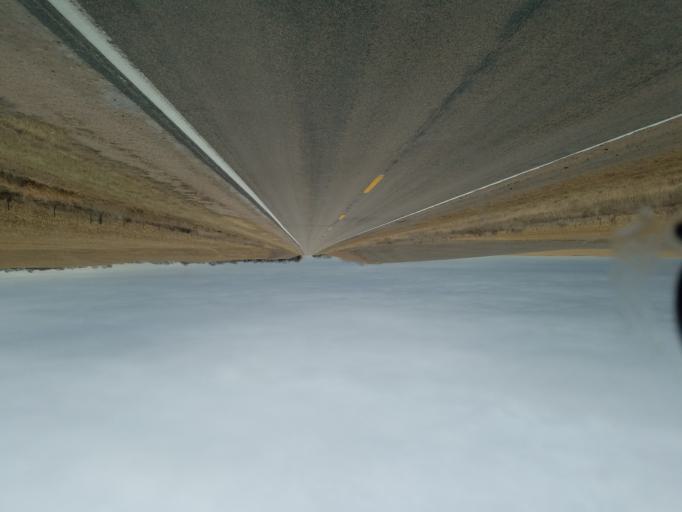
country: US
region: Nebraska
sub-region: Knox County
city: Bloomfield
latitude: 42.6128
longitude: -97.4564
